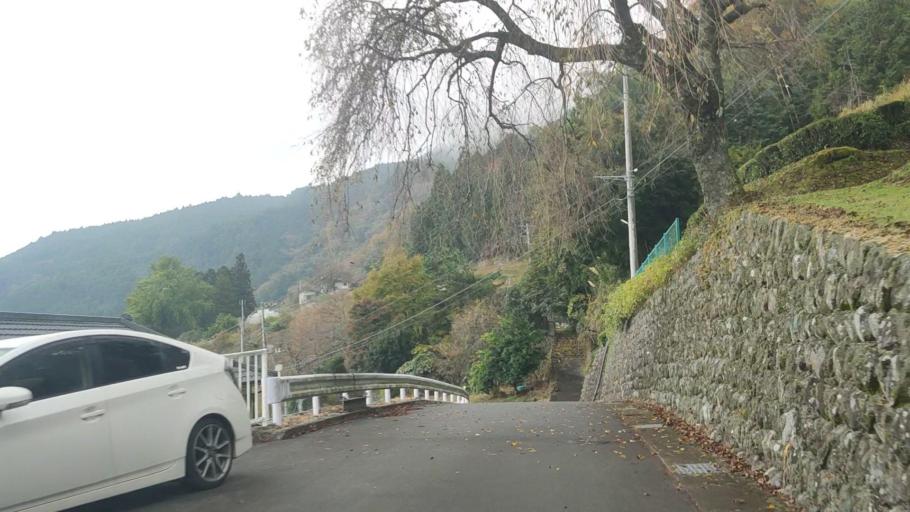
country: JP
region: Shizuoka
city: Fujinomiya
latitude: 35.3191
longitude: 138.4370
